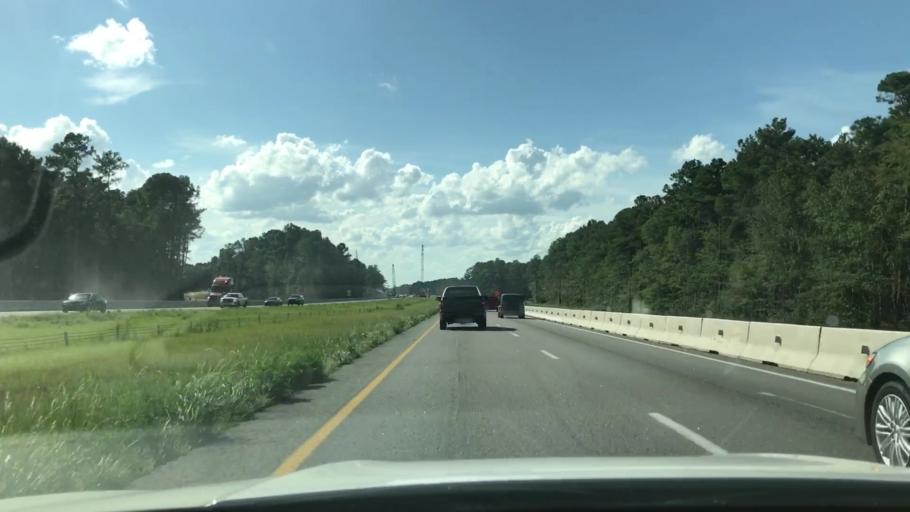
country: US
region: South Carolina
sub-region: Dorchester County
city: Ridgeville
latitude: 33.1173
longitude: -80.2703
